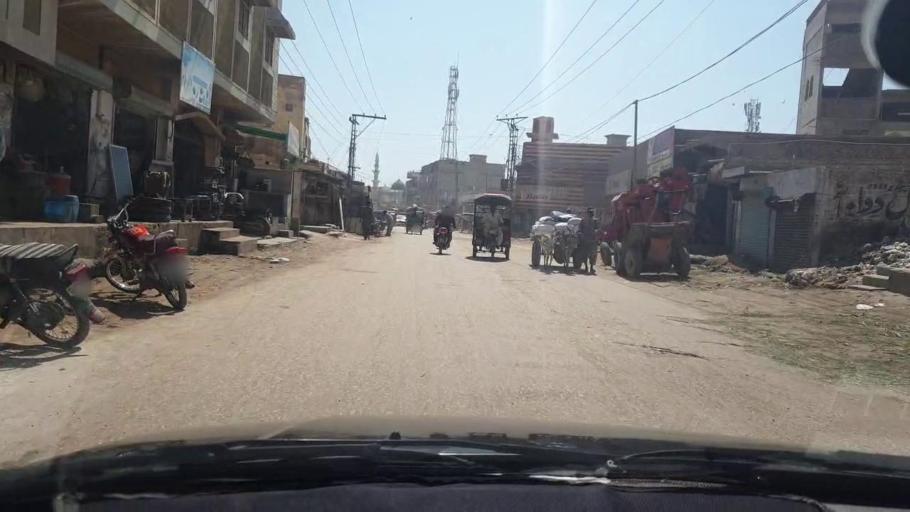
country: PK
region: Sindh
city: Tando Allahyar
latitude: 25.4587
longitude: 68.7177
